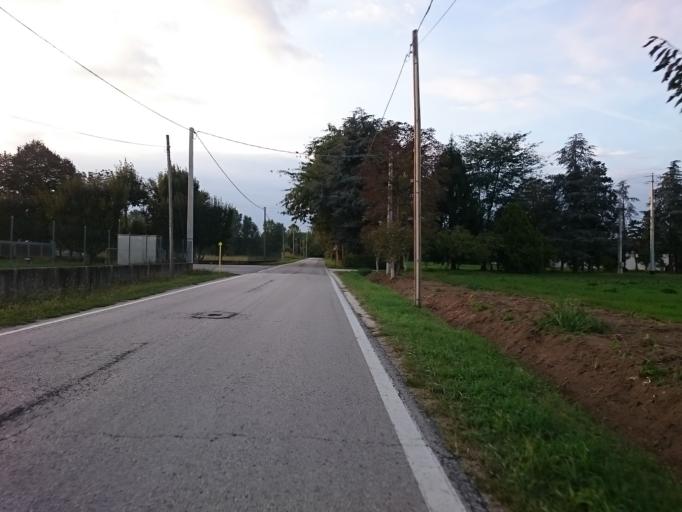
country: IT
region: Veneto
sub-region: Provincia di Vicenza
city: Grisignano di Zocco
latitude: 45.4879
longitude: 11.7206
